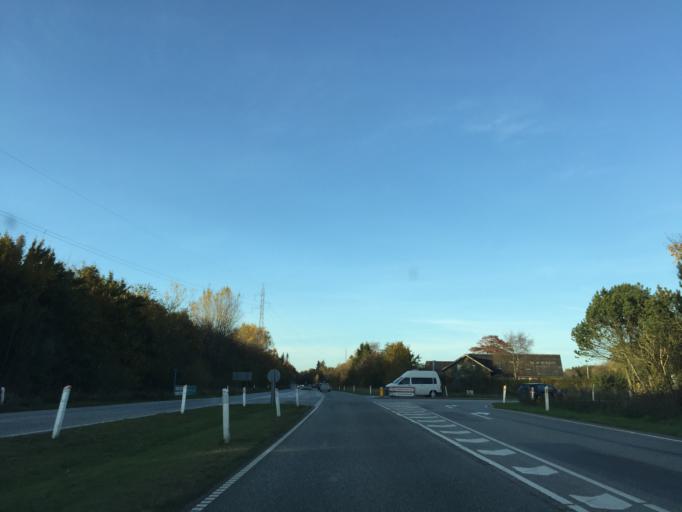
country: DK
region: South Denmark
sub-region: Aabenraa Kommune
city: Krusa
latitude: 54.8606
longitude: 9.4032
